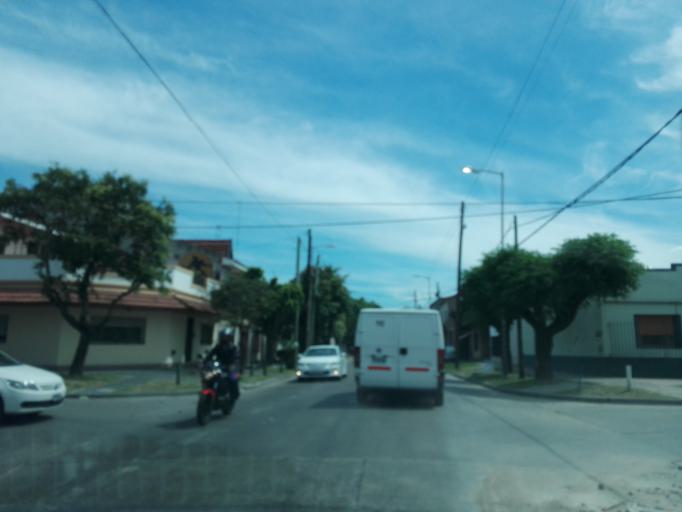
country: AR
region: Buenos Aires
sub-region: Partido de Avellaneda
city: Avellaneda
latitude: -34.6862
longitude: -58.3485
